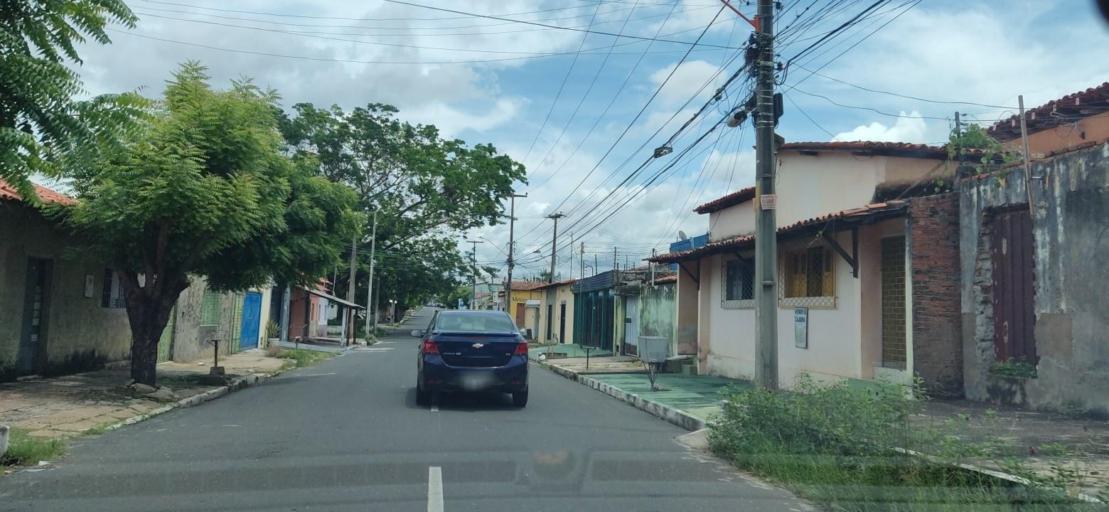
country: BR
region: Piaui
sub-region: Teresina
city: Teresina
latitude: -5.0753
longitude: -42.8052
